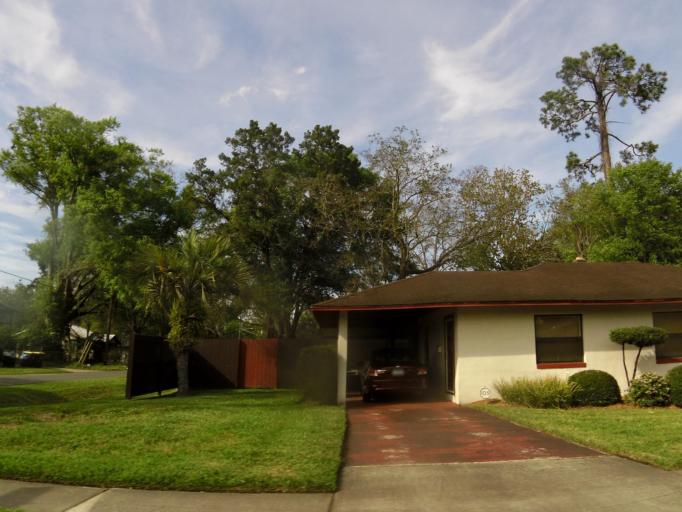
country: US
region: Florida
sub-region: Duval County
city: Jacksonville
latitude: 30.3031
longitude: -81.7295
